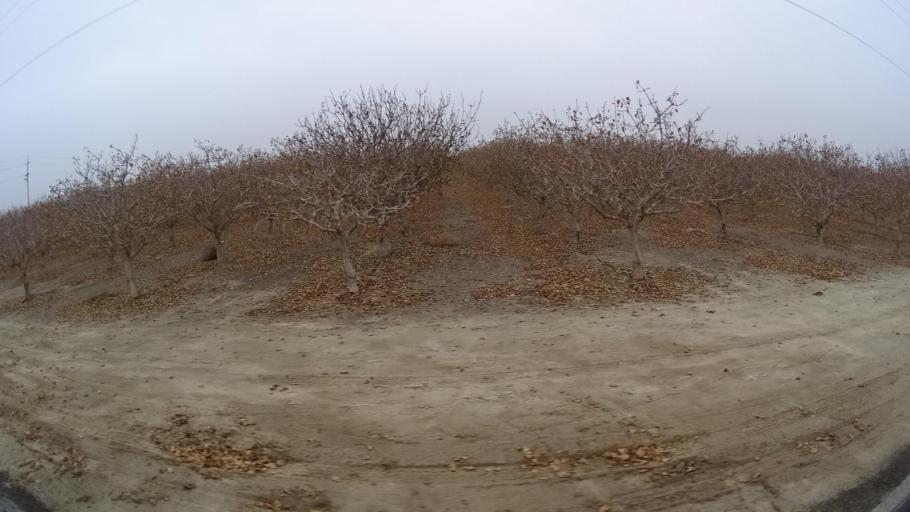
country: US
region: California
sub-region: Kern County
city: Lost Hills
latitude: 35.6023
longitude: -119.5805
